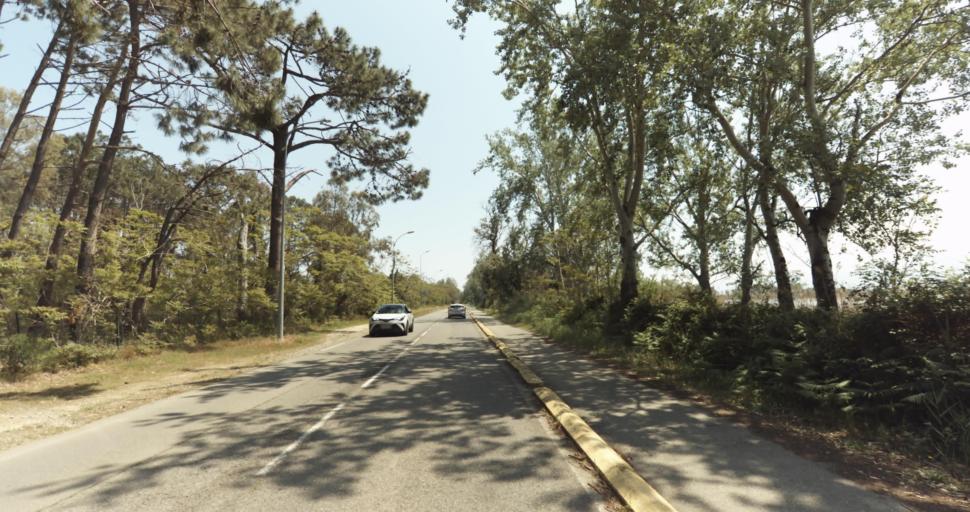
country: FR
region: Corsica
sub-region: Departement de la Haute-Corse
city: Biguglia
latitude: 42.6175
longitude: 9.4769
